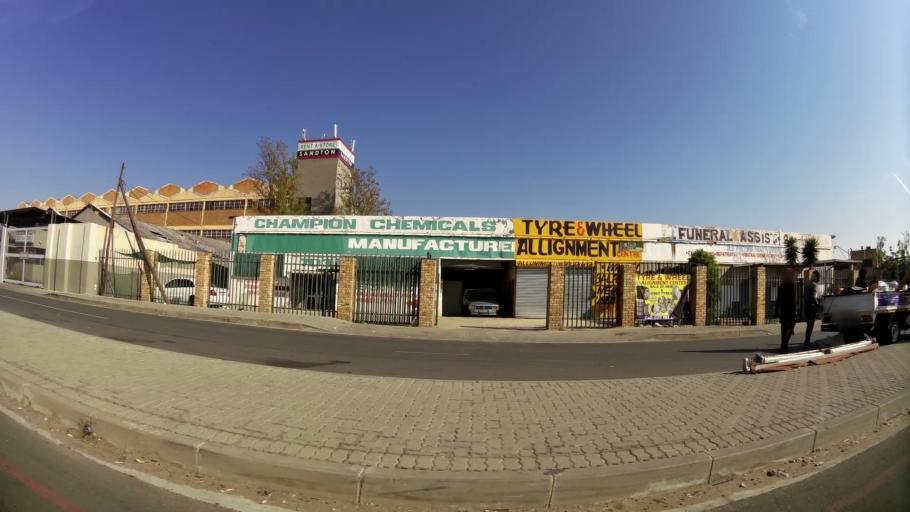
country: ZA
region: Gauteng
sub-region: City of Johannesburg Metropolitan Municipality
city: Modderfontein
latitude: -26.1021
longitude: 28.0855
